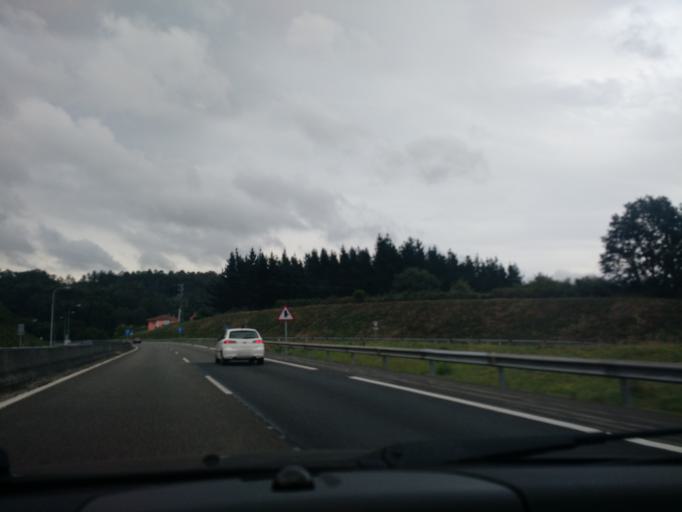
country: ES
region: Galicia
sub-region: Provincia da Coruna
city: Cambre
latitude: 43.3100
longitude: -8.3506
